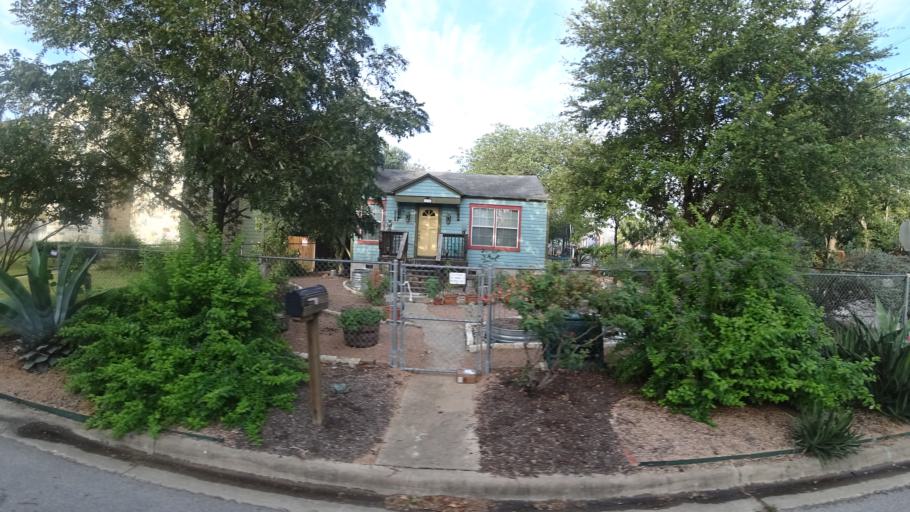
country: US
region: Texas
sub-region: Travis County
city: Austin
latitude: 30.2768
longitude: -97.7125
